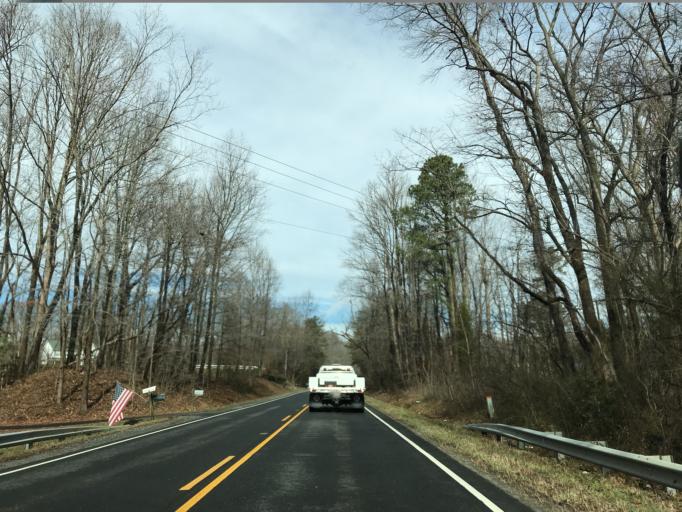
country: US
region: Virginia
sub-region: King George County
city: Dahlgren
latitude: 38.3127
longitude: -77.0783
